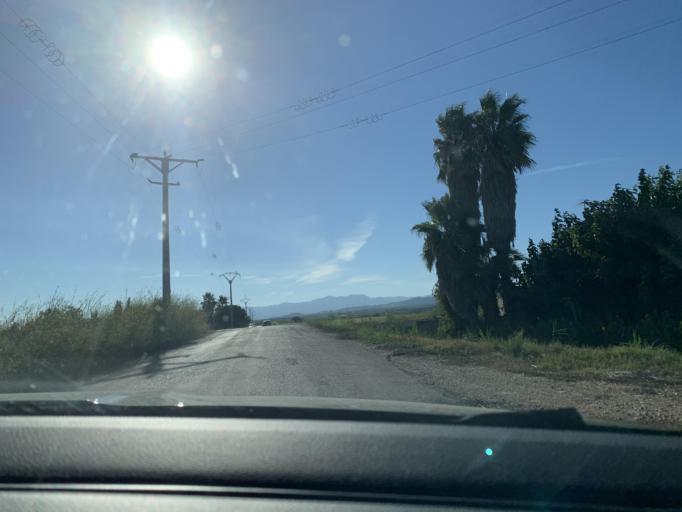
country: ES
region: Catalonia
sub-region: Provincia de Tarragona
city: L'Ampolla
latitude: 40.7708
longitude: 0.7090
